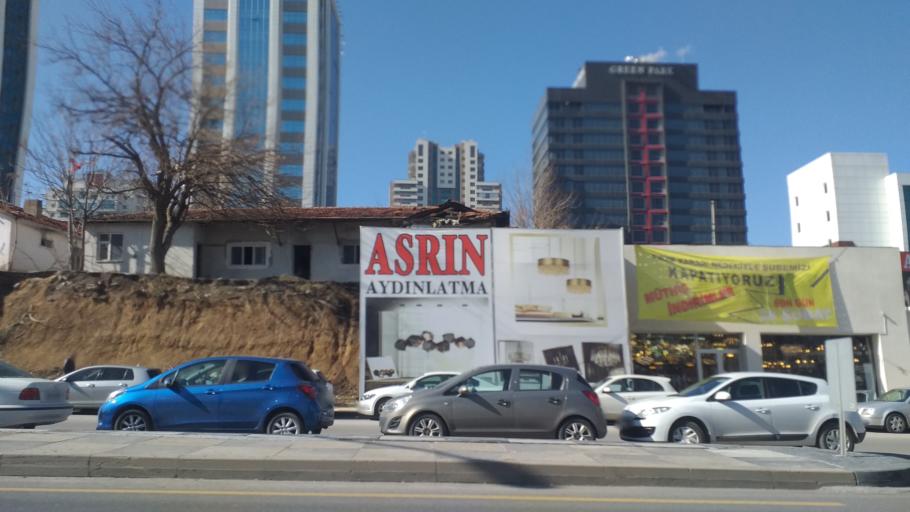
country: TR
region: Ankara
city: Ankara
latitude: 39.9026
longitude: 32.8140
